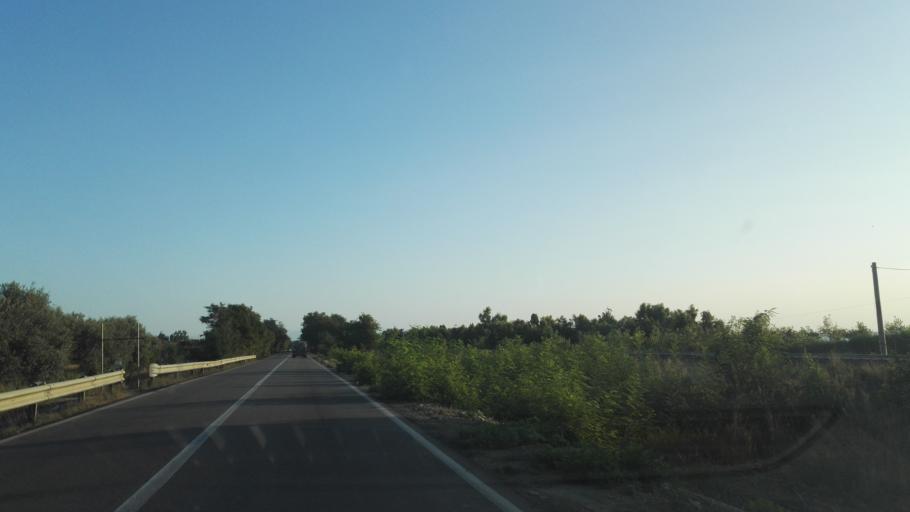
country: IT
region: Calabria
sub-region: Provincia di Catanzaro
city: Santa Caterina dello Ionio Marina
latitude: 38.5454
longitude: 16.5699
